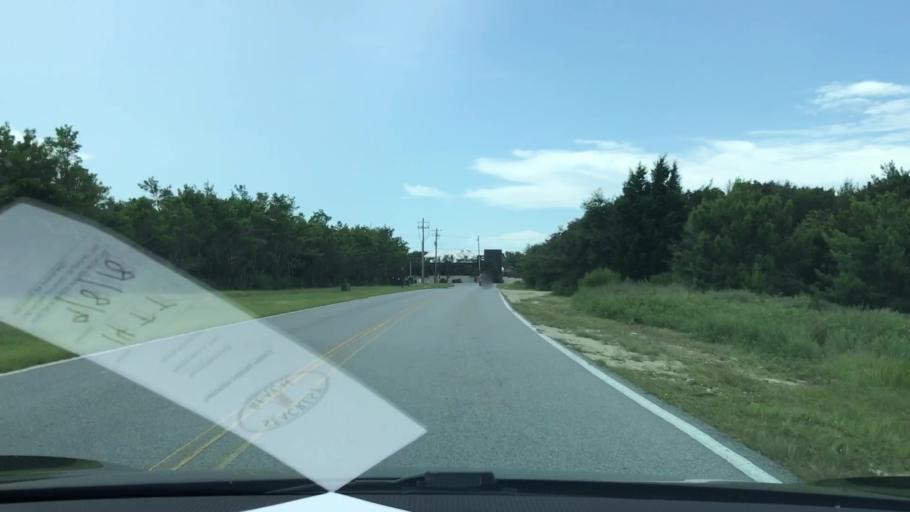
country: US
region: Florida
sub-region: Walton County
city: Seaside
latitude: 30.2887
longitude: -86.0367
